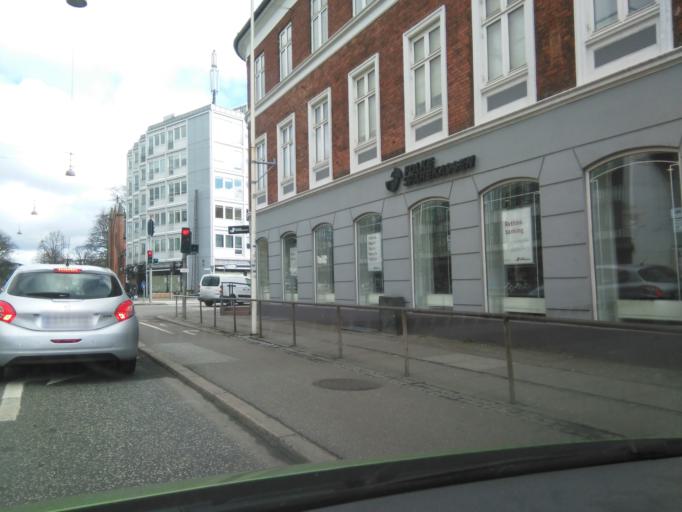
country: DK
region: Central Jutland
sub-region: Arhus Kommune
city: Arhus
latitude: 56.1503
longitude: 10.1993
